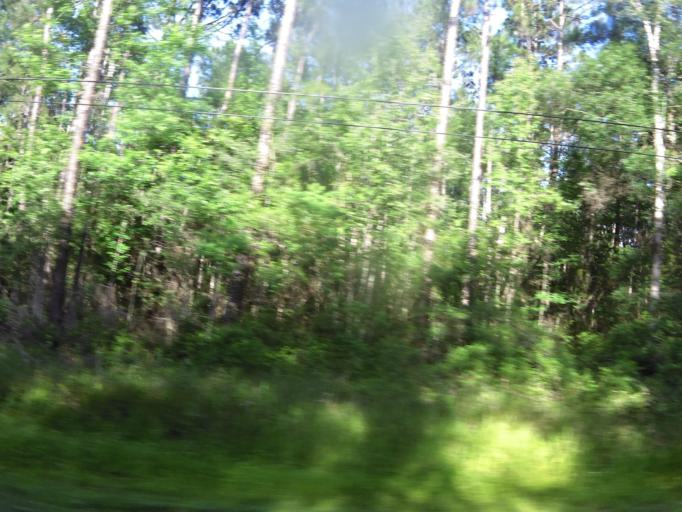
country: US
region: Florida
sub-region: Nassau County
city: Nassau Village-Ratliff
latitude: 30.4684
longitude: -81.7843
